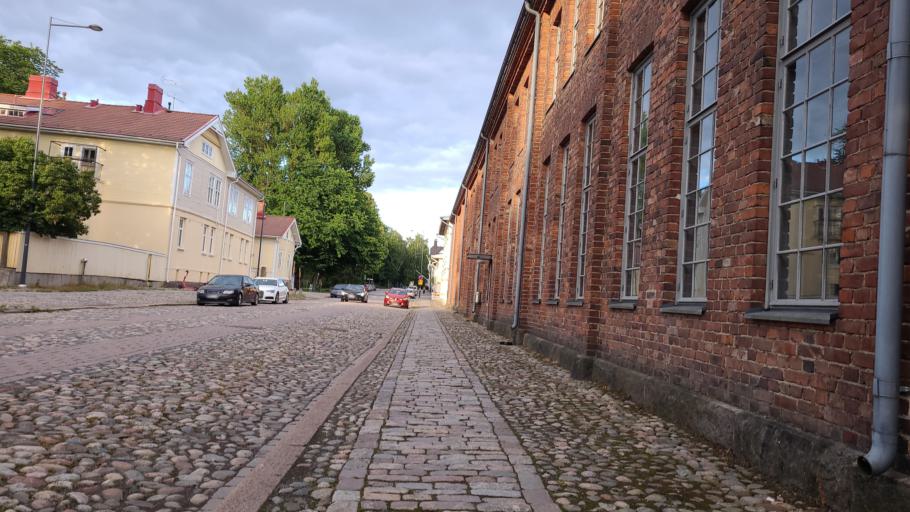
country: FI
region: Varsinais-Suomi
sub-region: Turku
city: Turku
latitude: 60.4576
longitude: 22.2789
